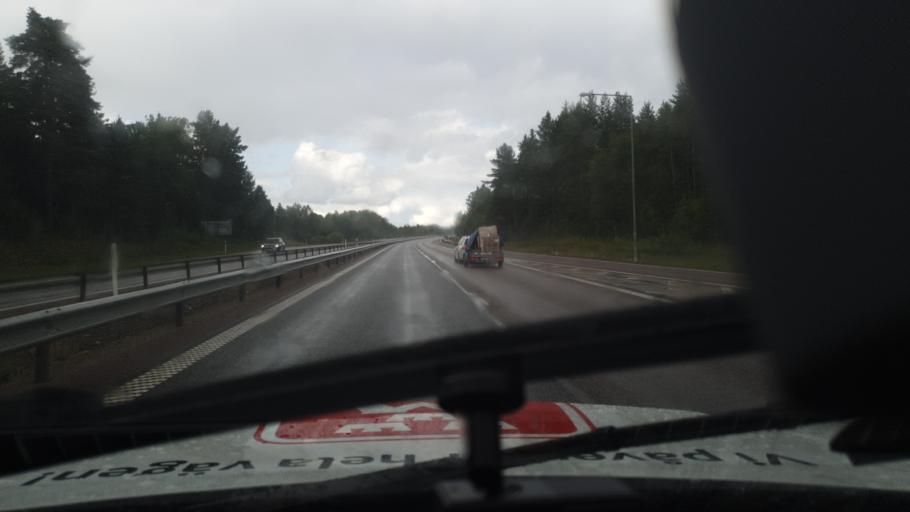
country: SE
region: Vaermland
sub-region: Grums Kommun
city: Slottsbron
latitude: 59.2866
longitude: 13.0467
